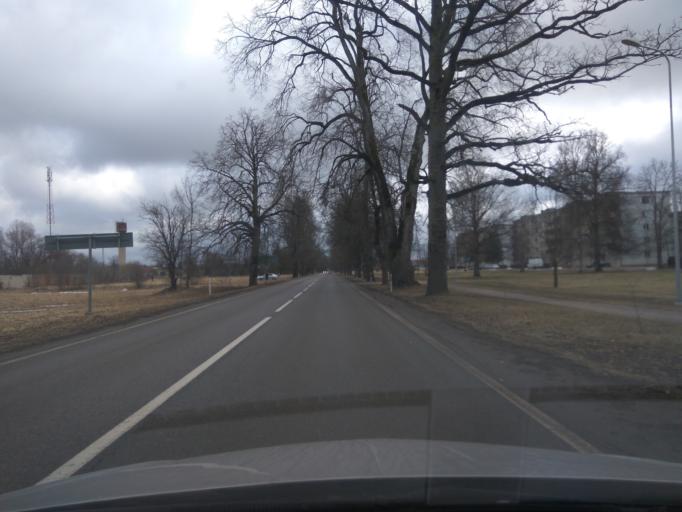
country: LV
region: Kuldigas Rajons
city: Kuldiga
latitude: 57.2765
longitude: 22.0233
